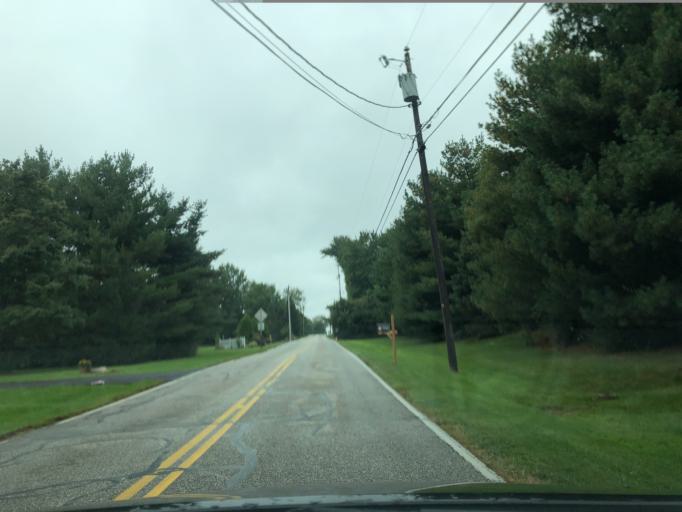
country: US
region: Ohio
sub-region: Hamilton County
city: Loveland
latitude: 39.2427
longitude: -84.2359
